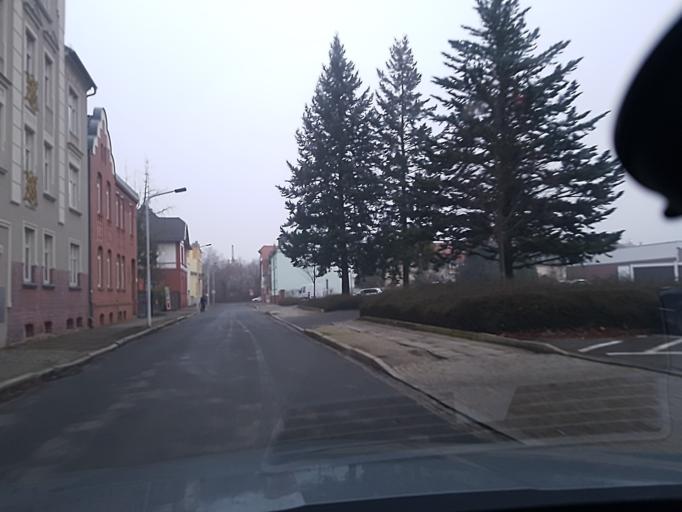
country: DE
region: Brandenburg
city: Finsterwalde
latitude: 51.6338
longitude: 13.7060
